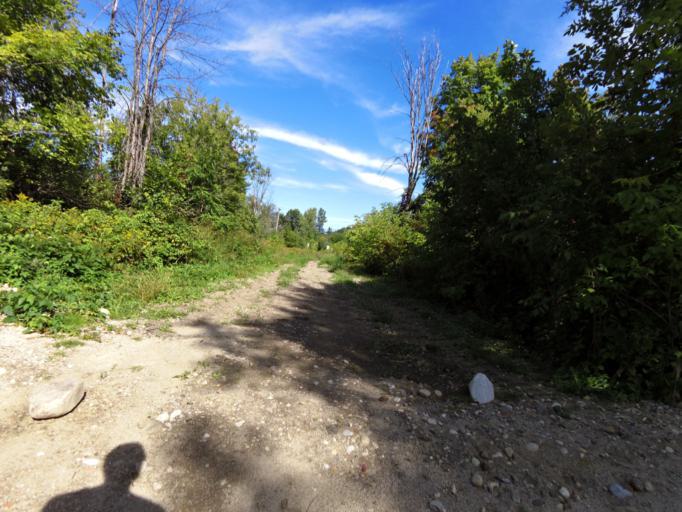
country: CA
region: Quebec
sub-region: Outaouais
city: Gatineau
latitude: 45.5068
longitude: -75.7817
